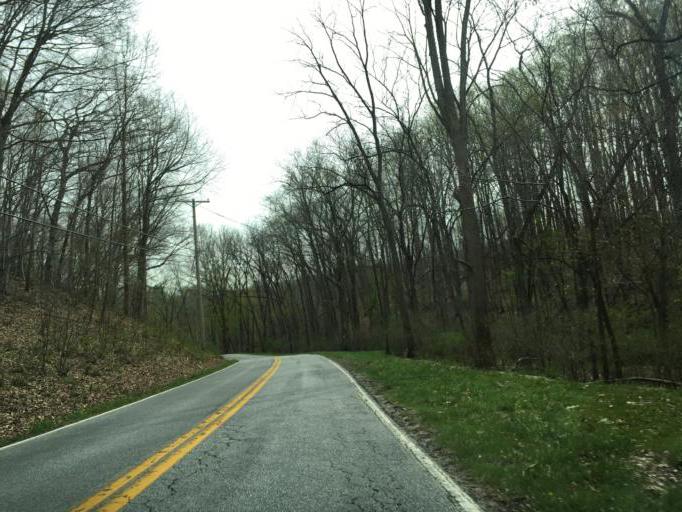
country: US
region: Maryland
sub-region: Baltimore County
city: Hunt Valley
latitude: 39.5224
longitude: -76.6166
